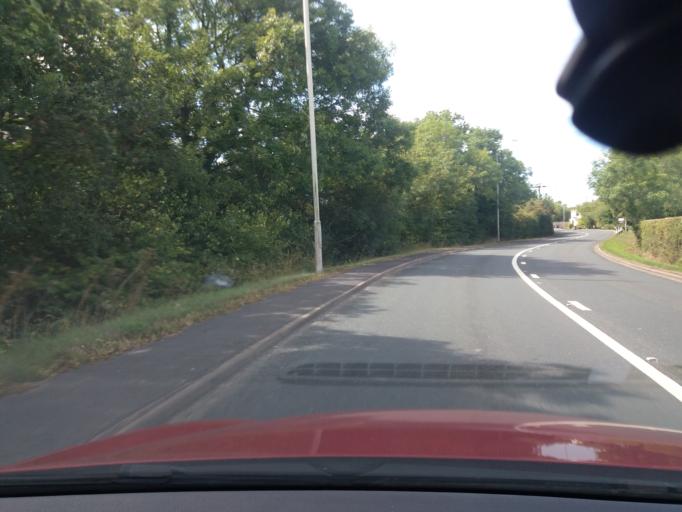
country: GB
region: England
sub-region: Lancashire
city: Coppull
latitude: 53.6336
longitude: -2.6821
